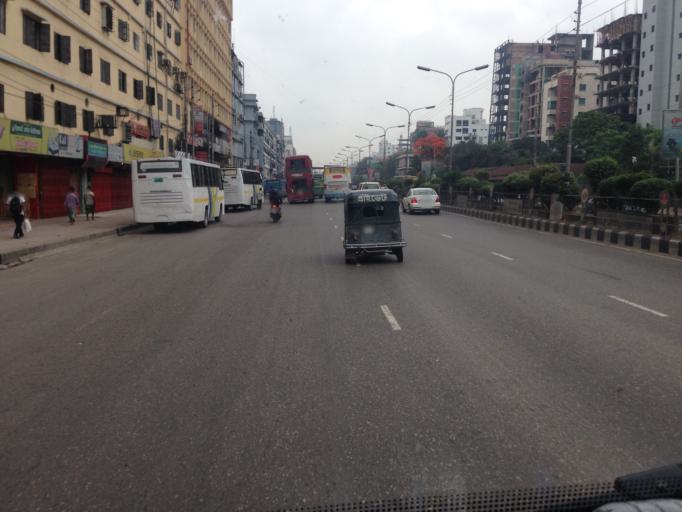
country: BD
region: Dhaka
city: Paltan
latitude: 23.7894
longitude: 90.4000
